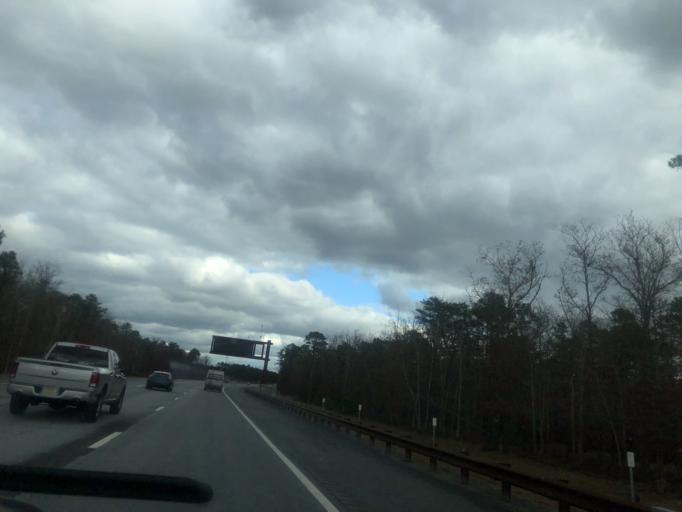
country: US
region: New Jersey
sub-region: Ocean County
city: Manahawkin
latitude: 39.6705
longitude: -74.3140
